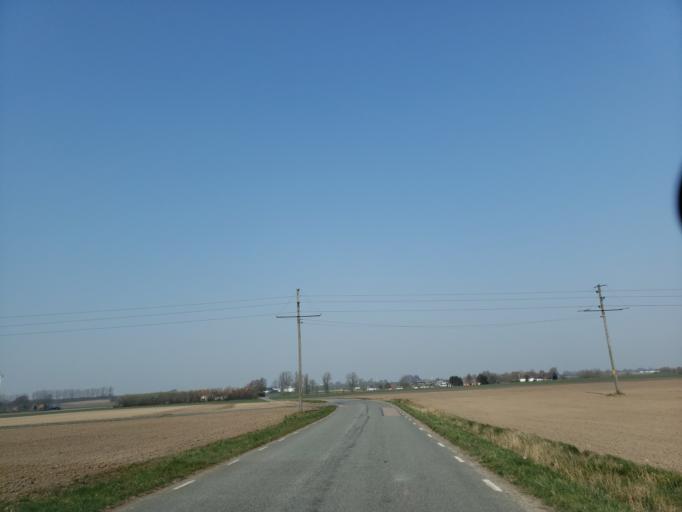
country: SE
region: Skane
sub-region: Simrishamns Kommun
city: Simrishamn
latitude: 55.4610
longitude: 14.2113
